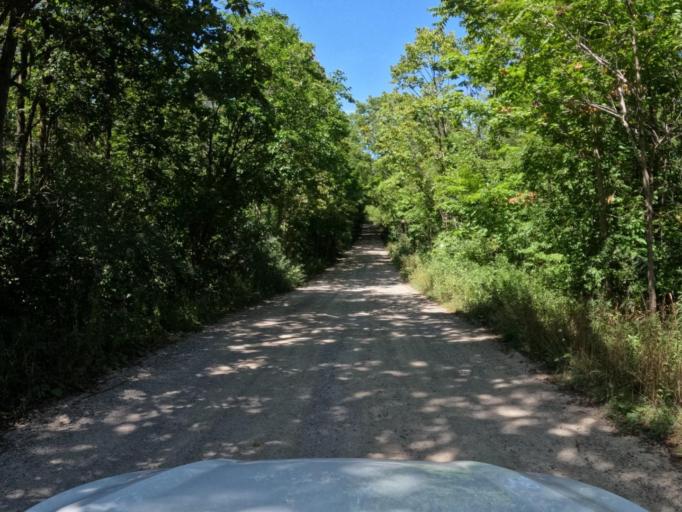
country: CA
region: Ontario
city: Cambridge
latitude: 43.4074
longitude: -80.2564
